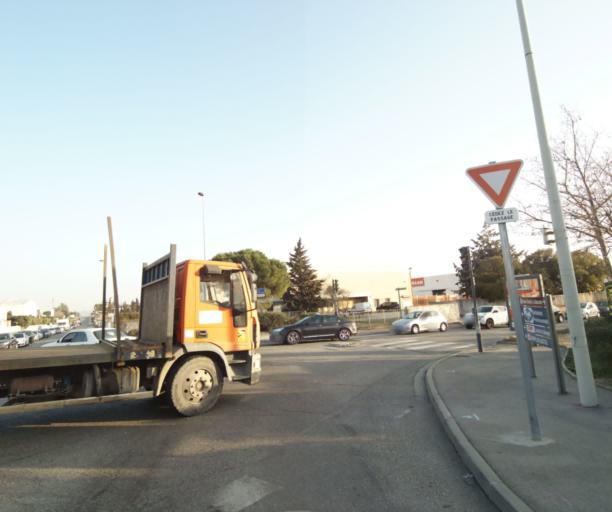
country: FR
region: Provence-Alpes-Cote d'Azur
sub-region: Departement des Bouches-du-Rhone
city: Vitrolles
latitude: 43.4397
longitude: 5.2424
